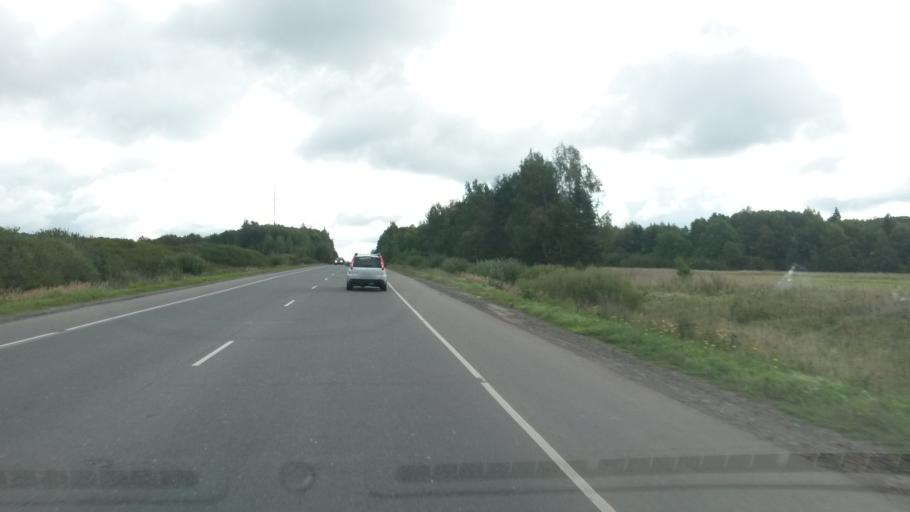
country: RU
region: Ivanovo
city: Rodniki
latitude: 57.0883
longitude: 41.6623
